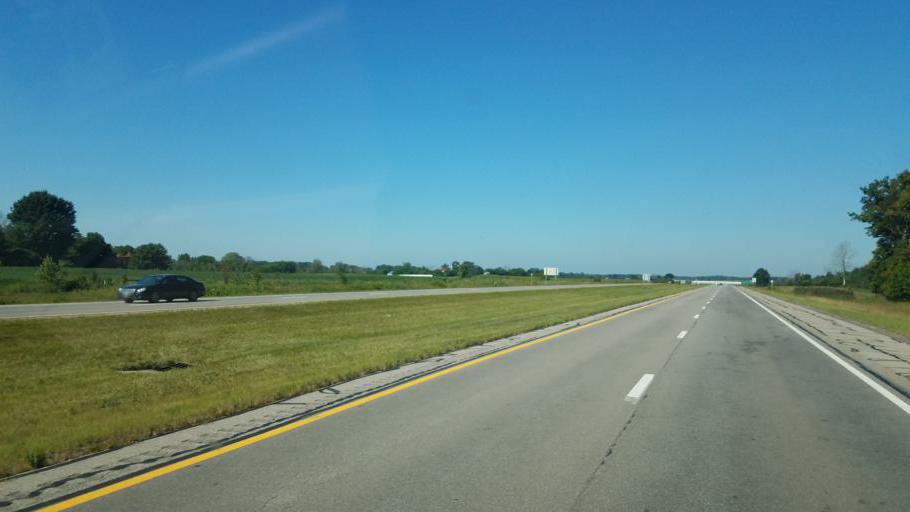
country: US
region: Ohio
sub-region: Crawford County
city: Galion
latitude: 40.7625
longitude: -82.8048
